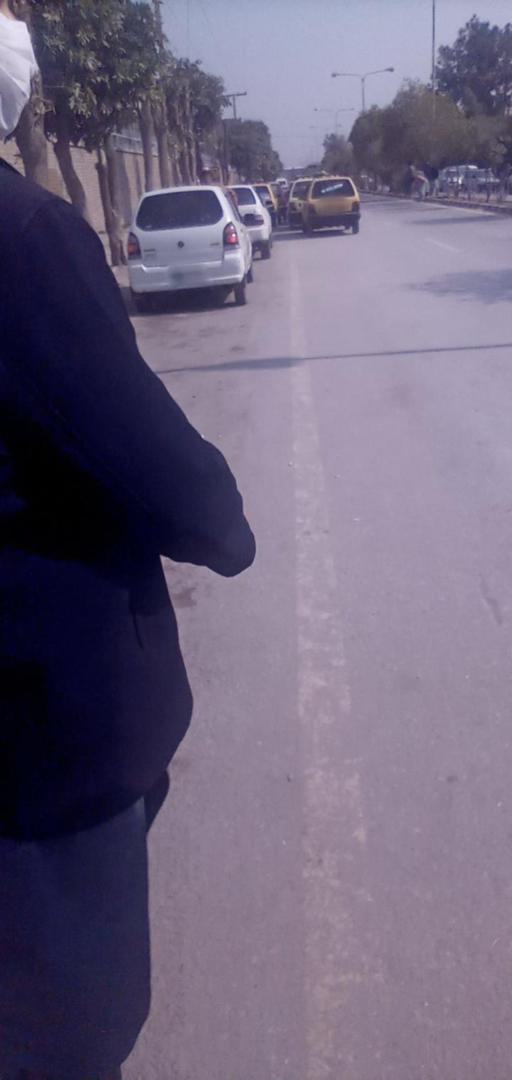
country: PK
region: Khyber Pakhtunkhwa
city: Peshawar
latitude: 33.9926
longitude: 71.4393
